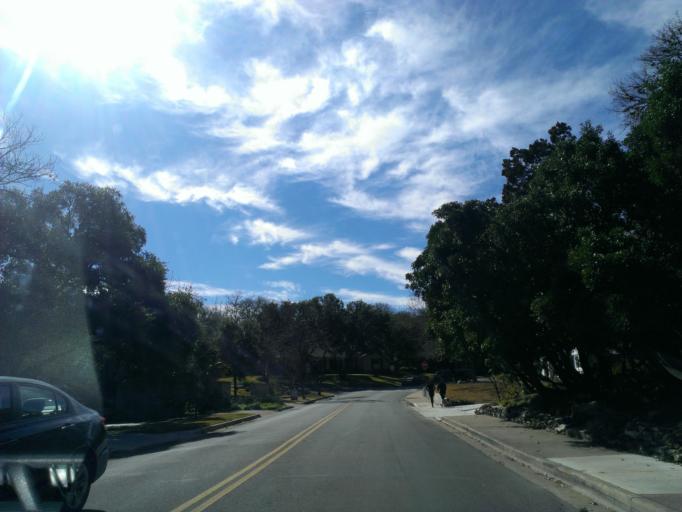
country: US
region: Texas
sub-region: Travis County
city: West Lake Hills
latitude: 30.3036
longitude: -97.7705
